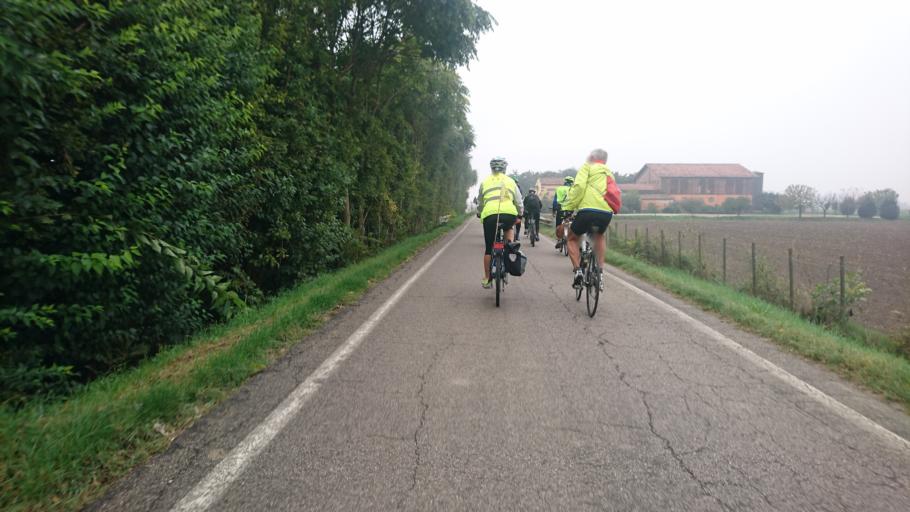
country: IT
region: Veneto
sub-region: Provincia di Padova
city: Pozzonovo
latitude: 45.1621
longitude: 11.7877
